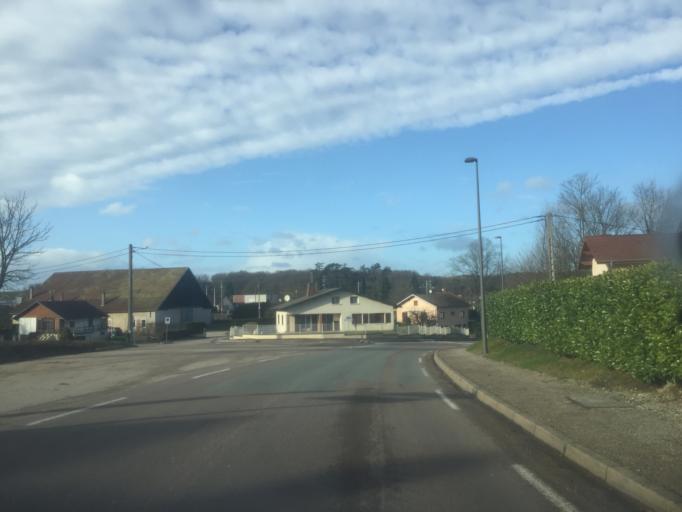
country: FR
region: Franche-Comte
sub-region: Departement du Doubs
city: Saint-Vit
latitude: 47.1831
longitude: 5.8126
